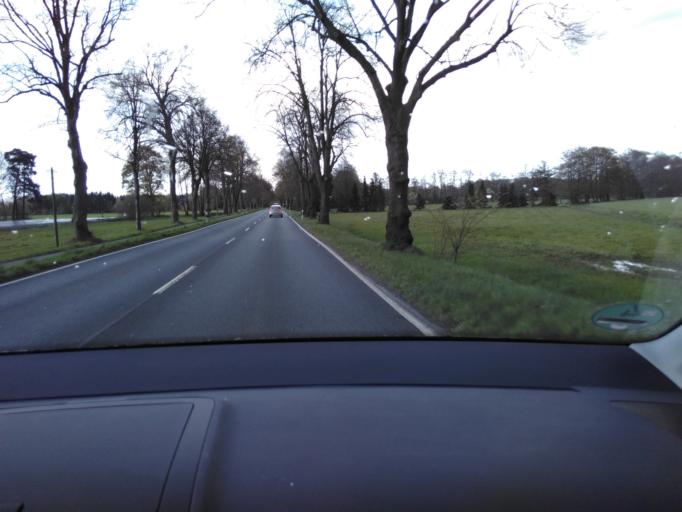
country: DE
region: North Rhine-Westphalia
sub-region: Regierungsbezirk Detmold
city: Steinhagen
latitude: 51.9485
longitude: 8.4347
